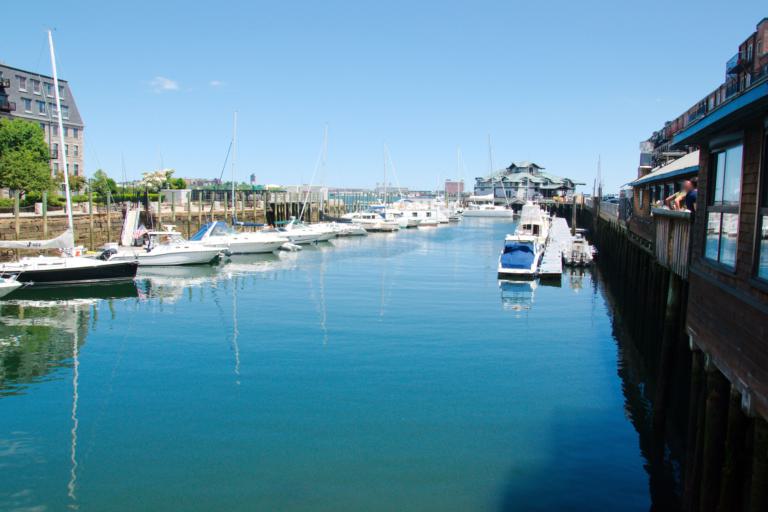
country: US
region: Massachusetts
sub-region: Suffolk County
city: Boston
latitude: 42.3631
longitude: -71.0510
